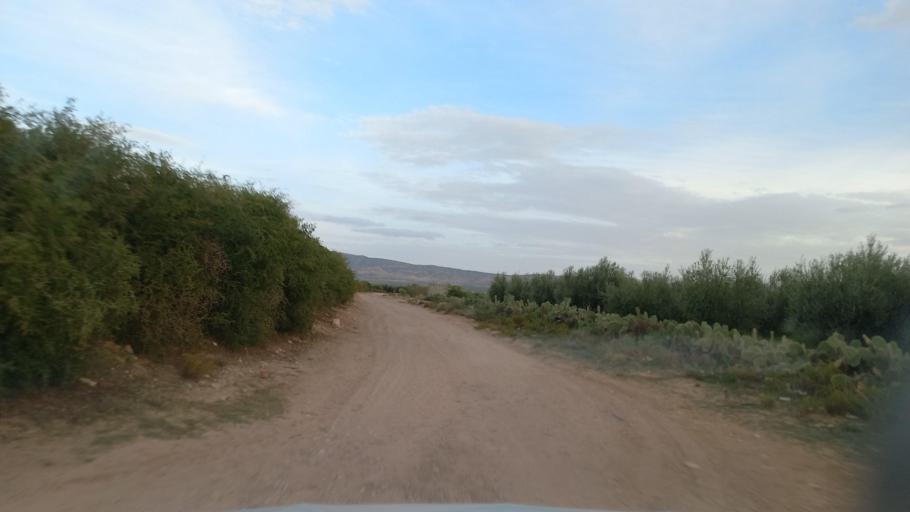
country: TN
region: Al Qasrayn
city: Sbiba
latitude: 35.4223
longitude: 9.1055
